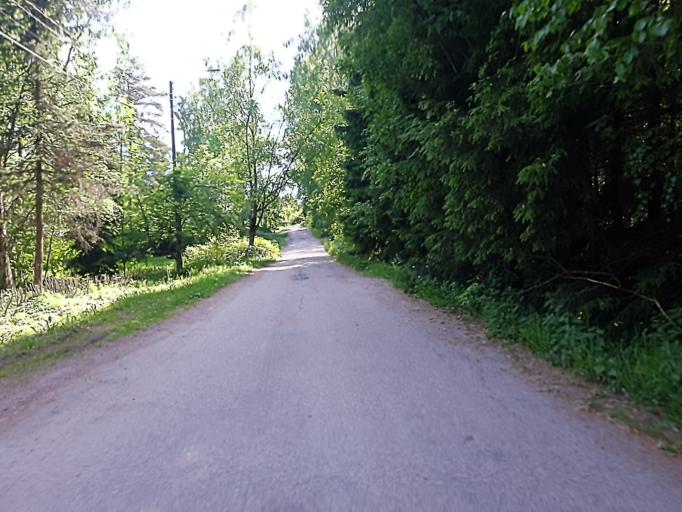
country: FI
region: Uusimaa
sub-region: Helsinki
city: Vantaa
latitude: 60.2933
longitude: 24.9172
